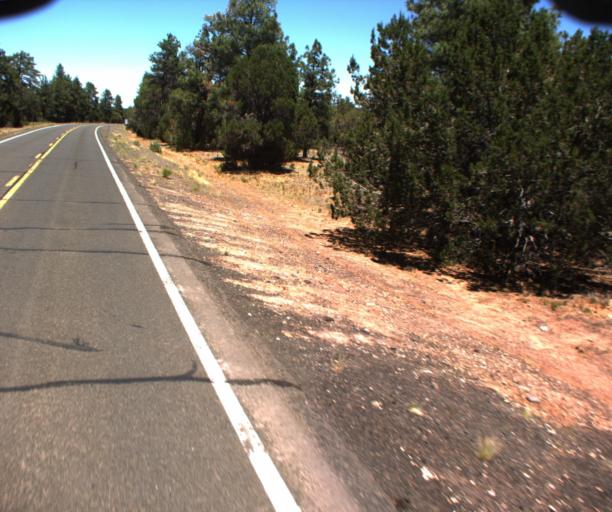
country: US
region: Arizona
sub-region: Gila County
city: Star Valley
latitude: 34.6810
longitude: -111.1126
